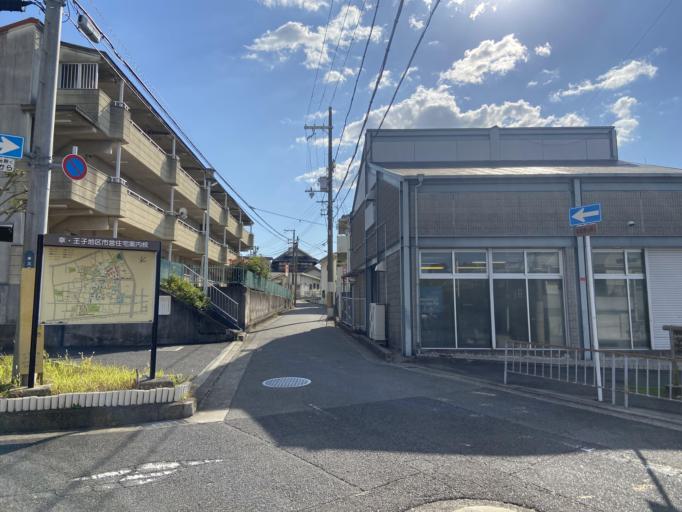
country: JP
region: Osaka
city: Takaishi
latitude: 34.5013
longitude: 135.4397
